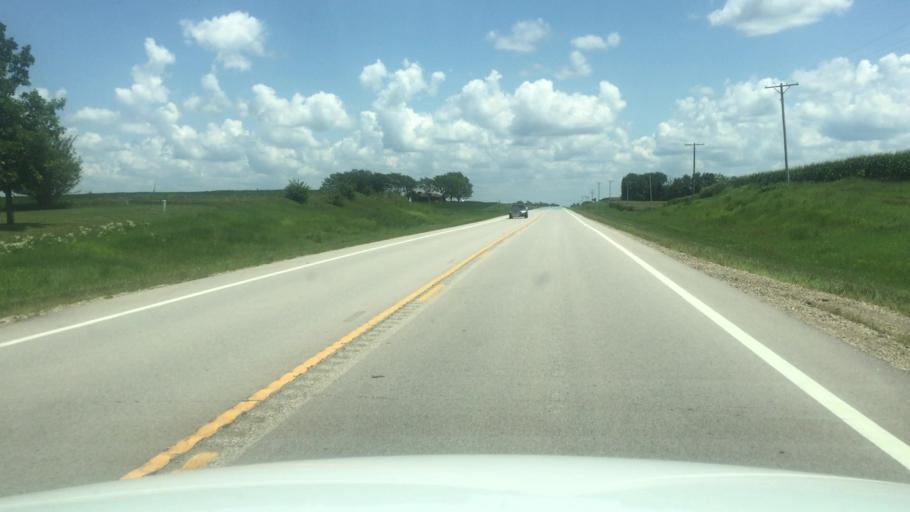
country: US
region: Kansas
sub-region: Brown County
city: Horton
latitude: 39.6672
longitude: -95.4661
